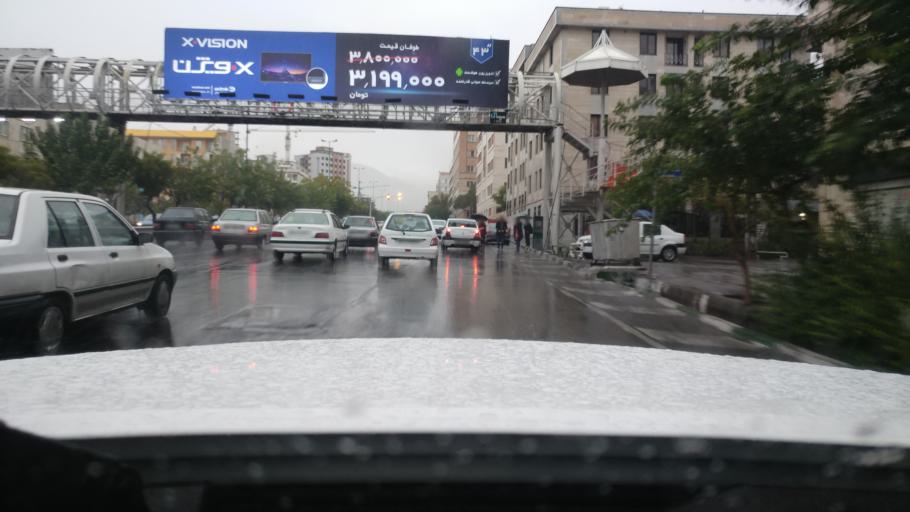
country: IR
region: Tehran
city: Tehran
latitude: 35.7214
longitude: 51.3085
